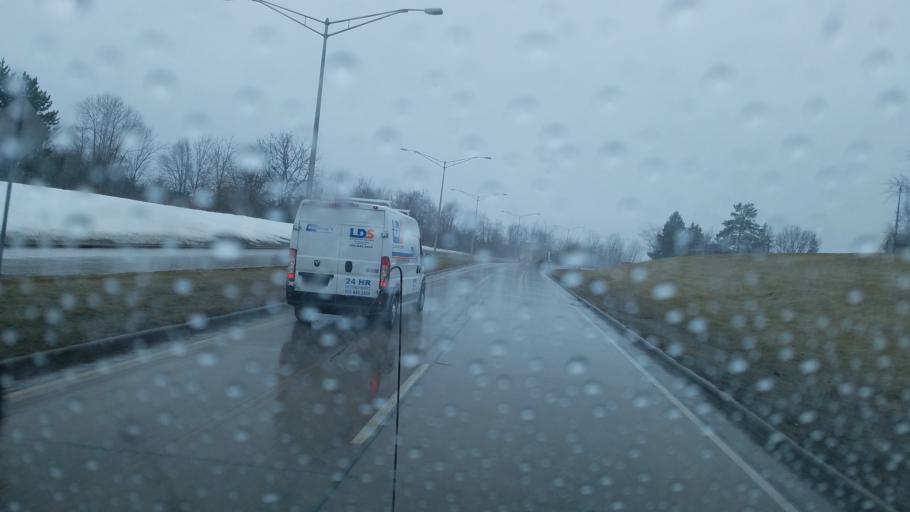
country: US
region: Wisconsin
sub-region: Wood County
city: Marshfield
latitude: 44.6721
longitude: -90.1834
